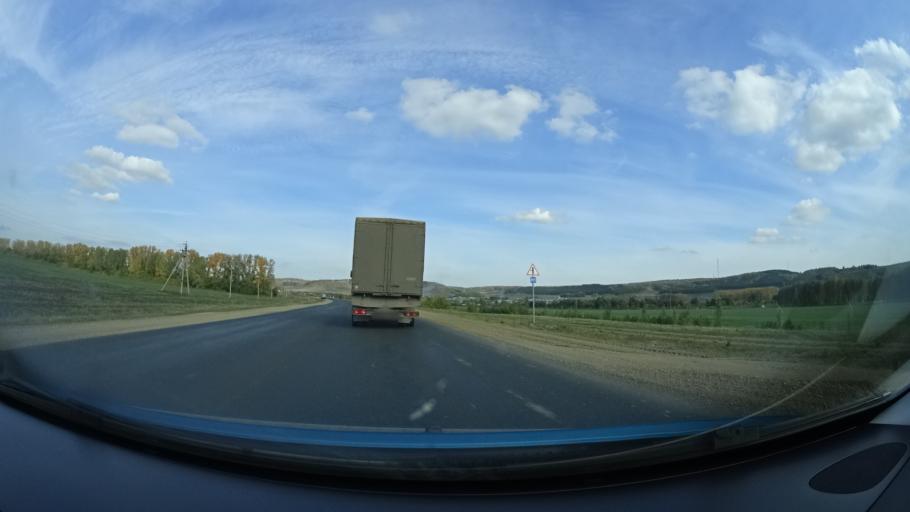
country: RU
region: Bashkortostan
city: Kandry
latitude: 54.5648
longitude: 54.2166
